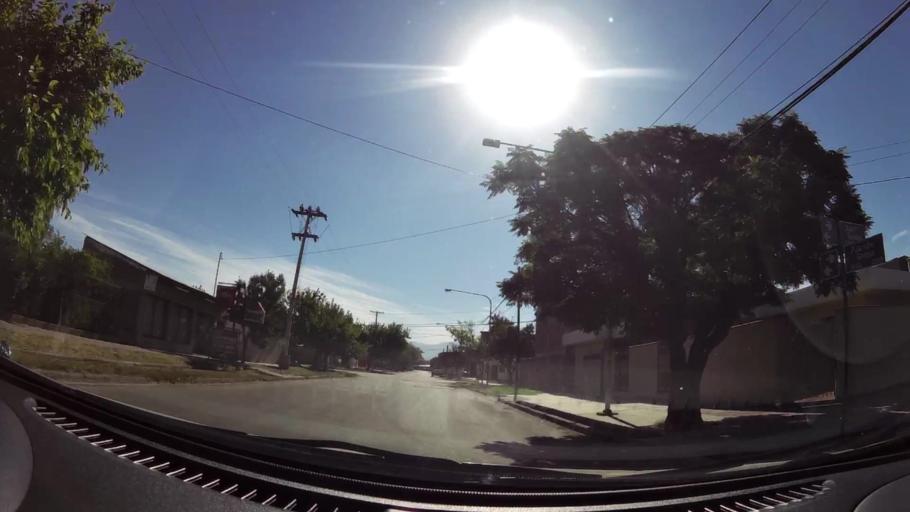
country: AR
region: Mendoza
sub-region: Departamento de Godoy Cruz
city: Godoy Cruz
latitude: -32.9414
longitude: -68.8062
